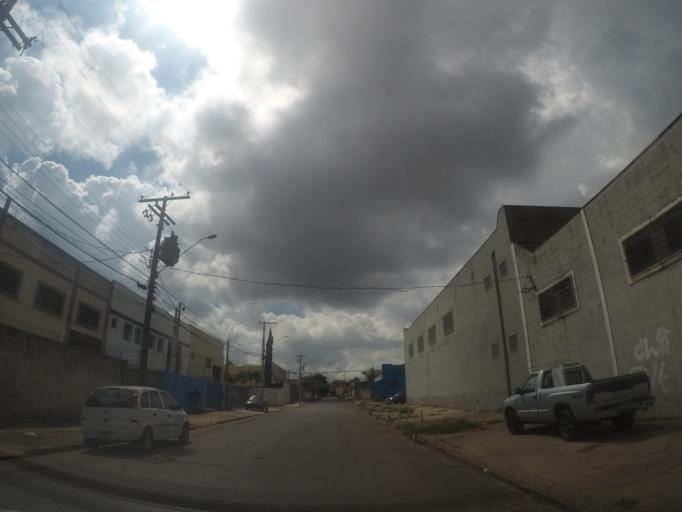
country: BR
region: Sao Paulo
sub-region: Hortolandia
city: Hortolandia
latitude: -22.8549
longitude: -47.1637
